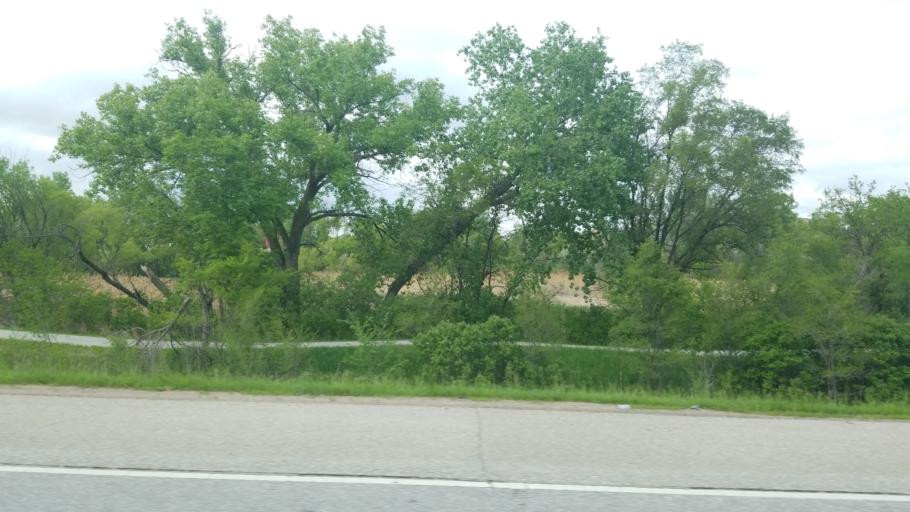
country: US
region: Nebraska
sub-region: Lancaster County
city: Lincoln
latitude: 40.8738
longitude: -96.7275
